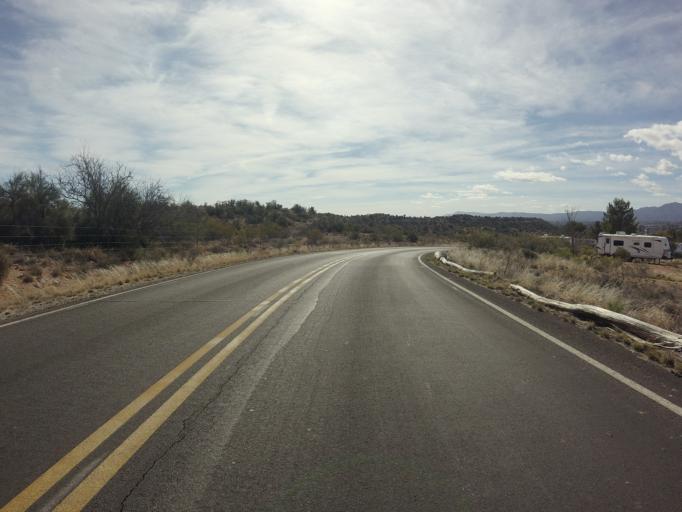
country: US
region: Arizona
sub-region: Yavapai County
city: Cottonwood
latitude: 34.7615
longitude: -112.0149
